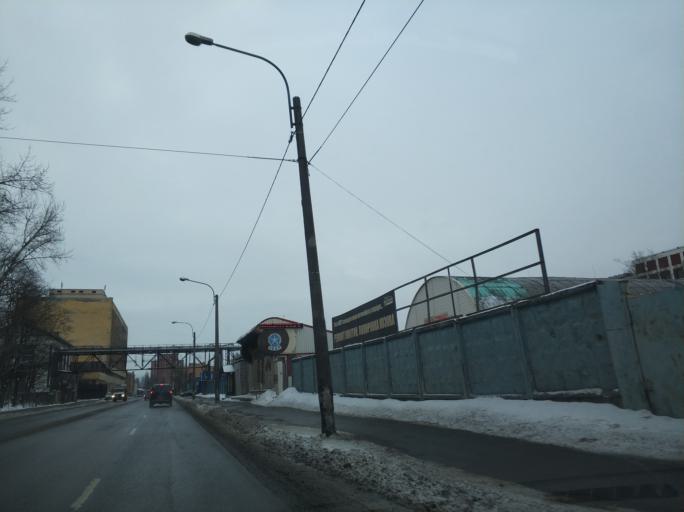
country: RU
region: St.-Petersburg
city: Centralniy
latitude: 59.9201
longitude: 30.3734
